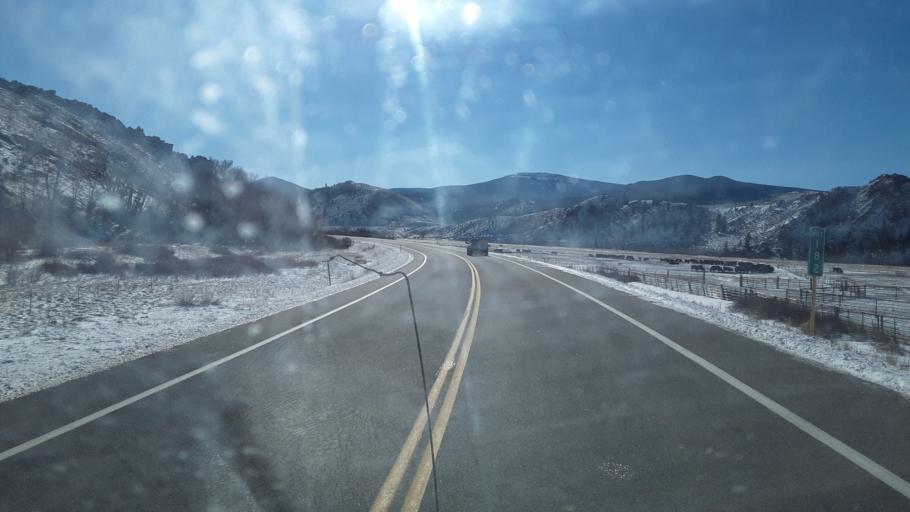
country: US
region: Colorado
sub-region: Gunnison County
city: Gunnison
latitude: 38.4193
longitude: -106.5234
